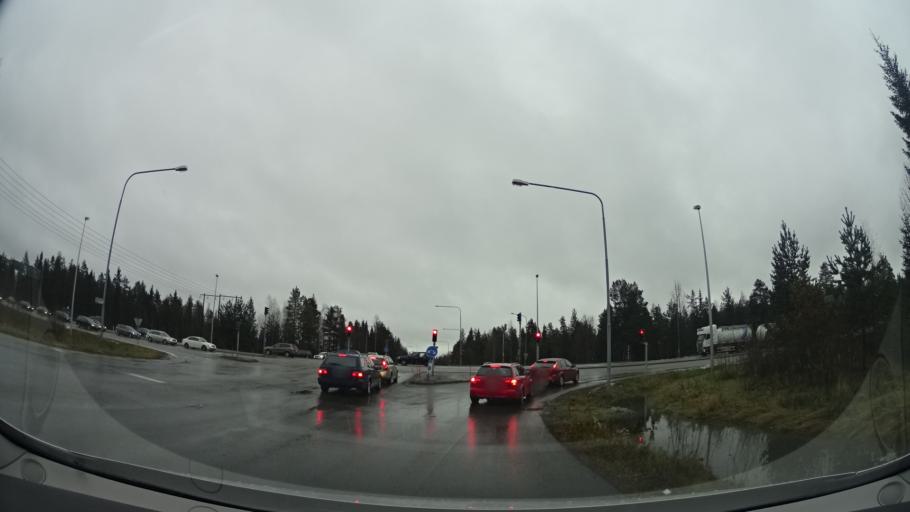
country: SE
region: Vaesterbotten
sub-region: Skelleftea Kommun
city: Skelleftea
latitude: 64.7625
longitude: 21.0038
